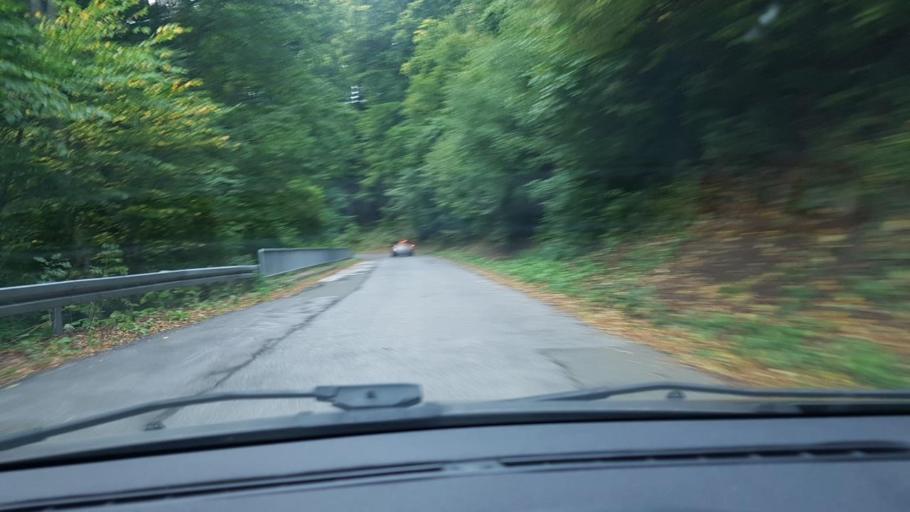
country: HR
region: Grad Zagreb
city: Kasina
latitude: 45.8904
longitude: 15.9373
